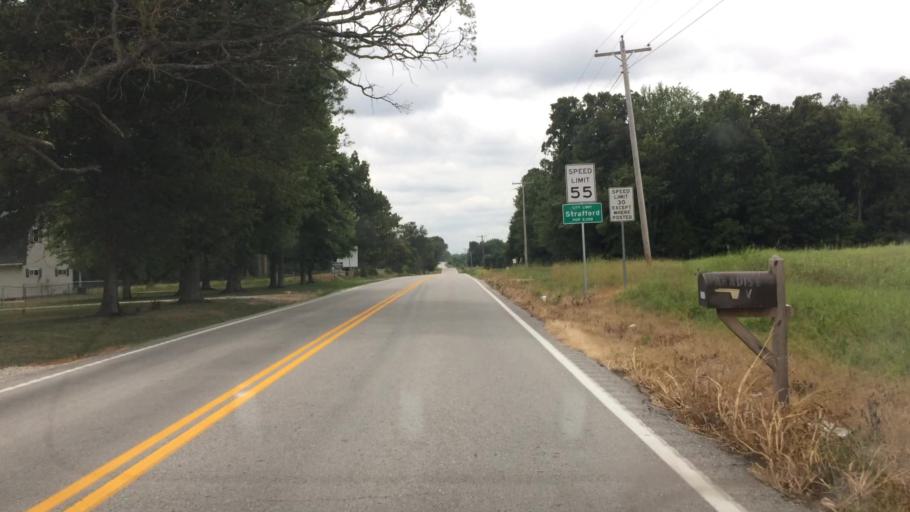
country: US
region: Missouri
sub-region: Greene County
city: Strafford
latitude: 37.2932
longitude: -93.1131
